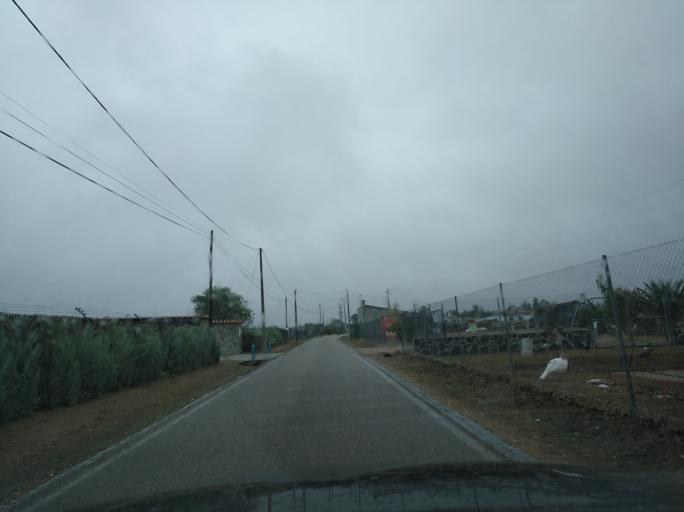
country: PT
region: Portalegre
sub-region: Campo Maior
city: Campo Maior
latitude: 38.9637
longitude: -7.0744
